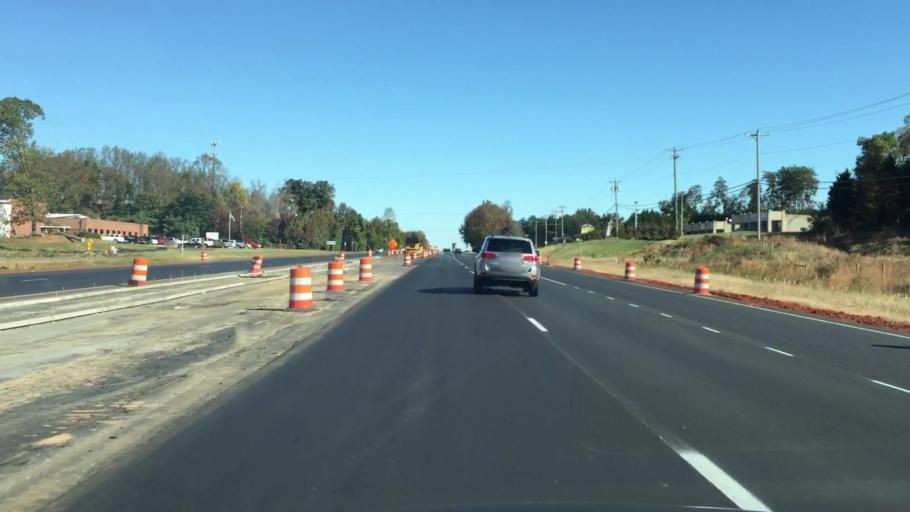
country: US
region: North Carolina
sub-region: Guilford County
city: McLeansville
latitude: 36.1601
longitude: -79.7229
